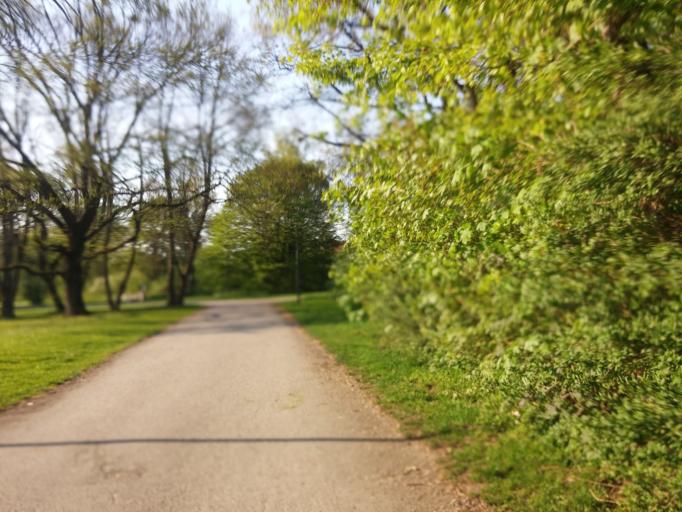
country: DE
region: Bavaria
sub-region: Upper Bavaria
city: Neubiberg
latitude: 48.1095
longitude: 11.6575
